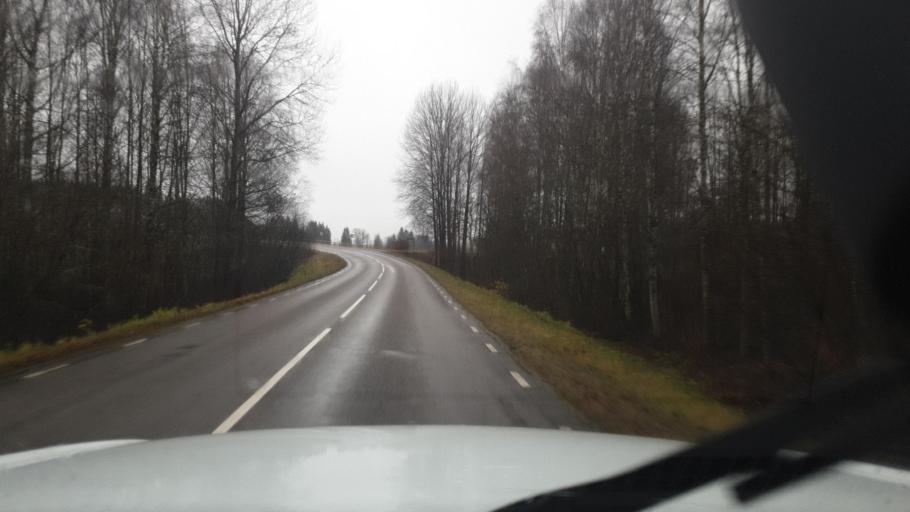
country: SE
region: Vaermland
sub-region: Sunne Kommun
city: Sunne
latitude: 59.7996
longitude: 13.0537
